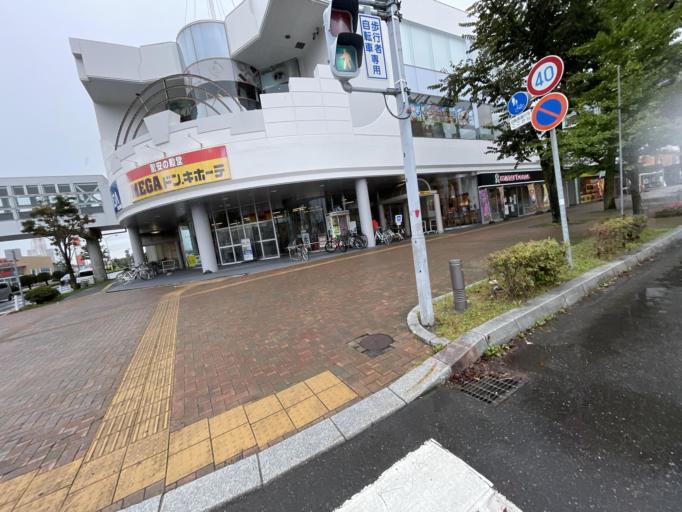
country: JP
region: Hokkaido
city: Tomakomai
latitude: 42.6410
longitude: 141.5965
